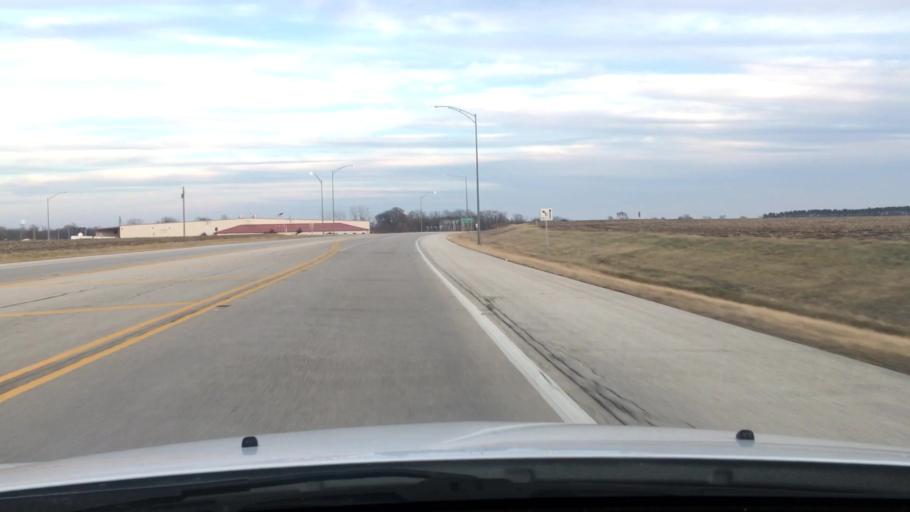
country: US
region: Illinois
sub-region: Livingston County
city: Chatsworth
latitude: 40.7508
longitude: -88.3132
